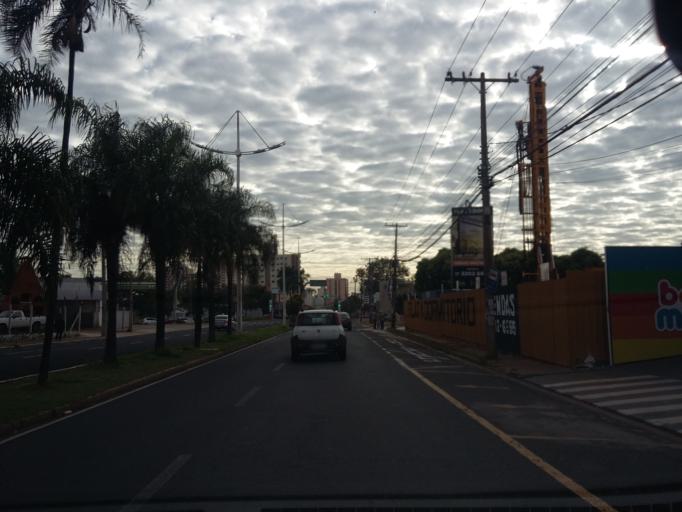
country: BR
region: Sao Paulo
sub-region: Sao Jose Do Rio Preto
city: Sao Jose do Rio Preto
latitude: -20.8248
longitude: -49.3939
